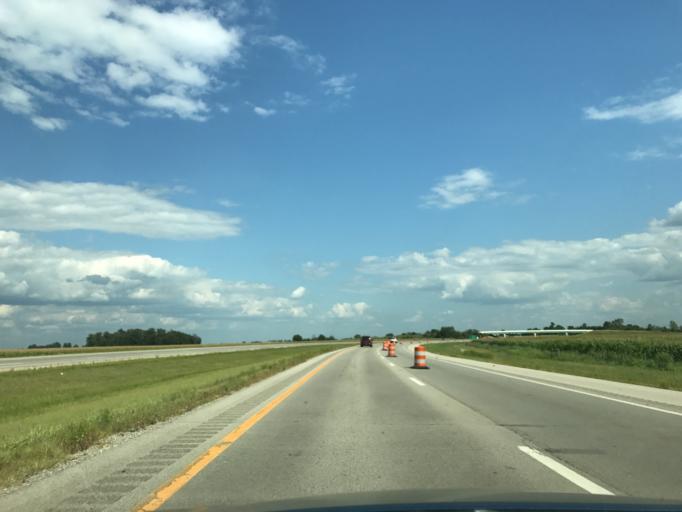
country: US
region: Ohio
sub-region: Van Wert County
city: Van Wert
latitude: 40.8852
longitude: -84.5365
